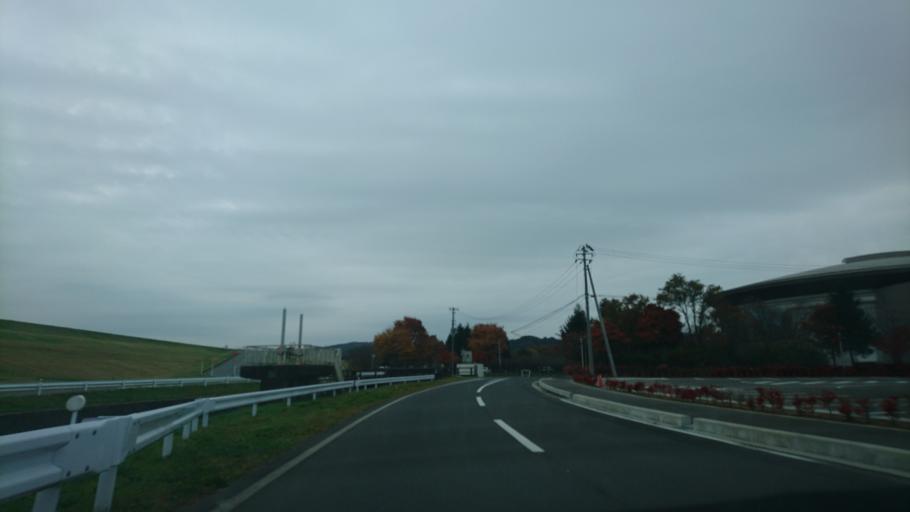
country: JP
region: Iwate
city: Ichinoseki
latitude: 38.9423
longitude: 141.1550
